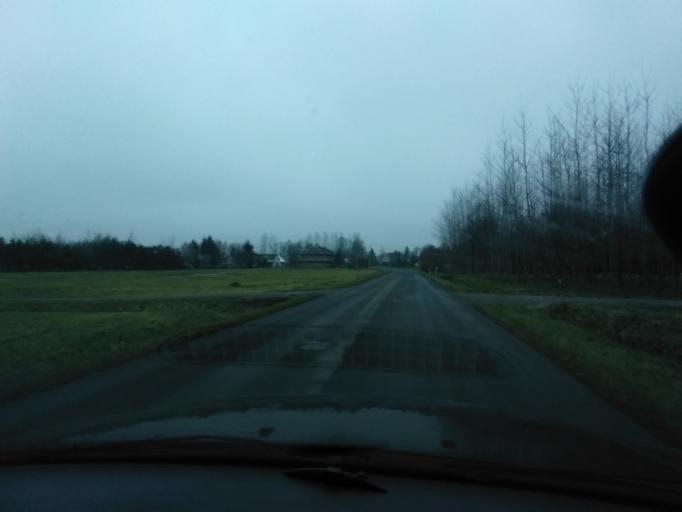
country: PL
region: Subcarpathian Voivodeship
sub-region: Powiat przeworski
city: Zarzecze
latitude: 49.9542
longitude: 22.5670
